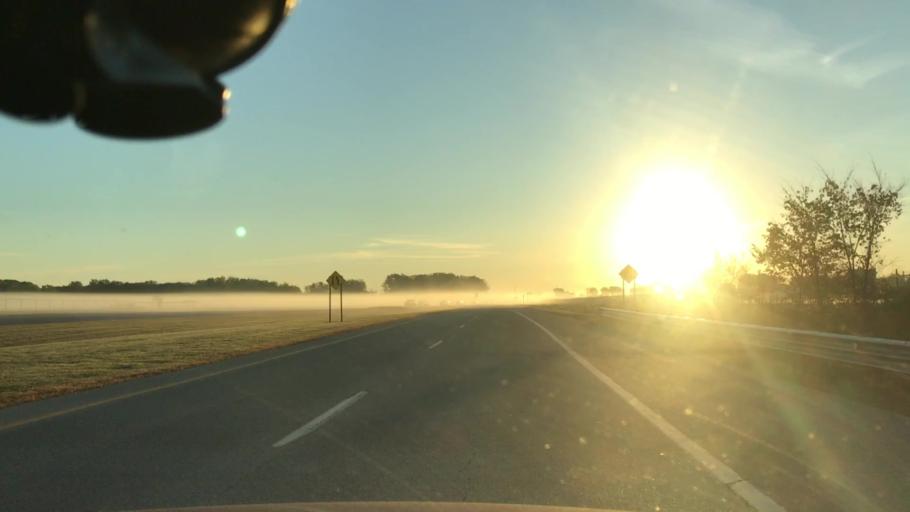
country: US
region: Michigan
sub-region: Macomb County
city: Mount Clemens
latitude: 42.6303
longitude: -82.8405
